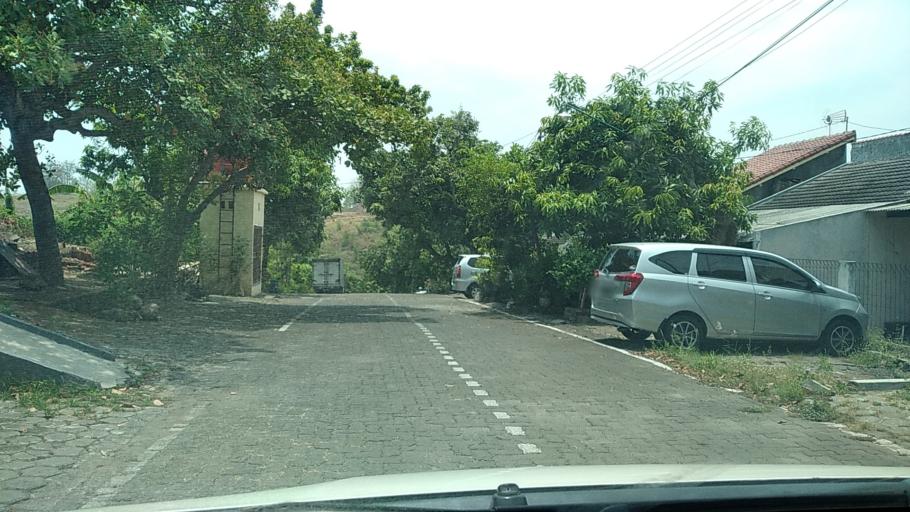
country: ID
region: Central Java
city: Mranggen
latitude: -7.0305
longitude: 110.4730
